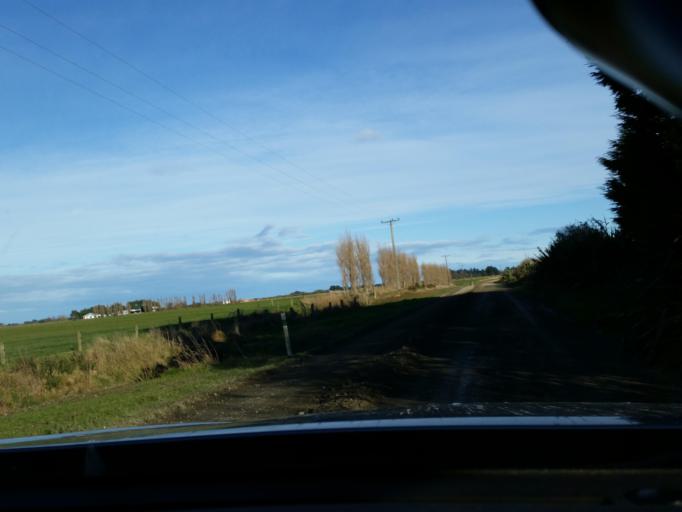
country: NZ
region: Southland
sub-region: Southland District
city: Winton
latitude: -46.2496
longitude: 168.4617
